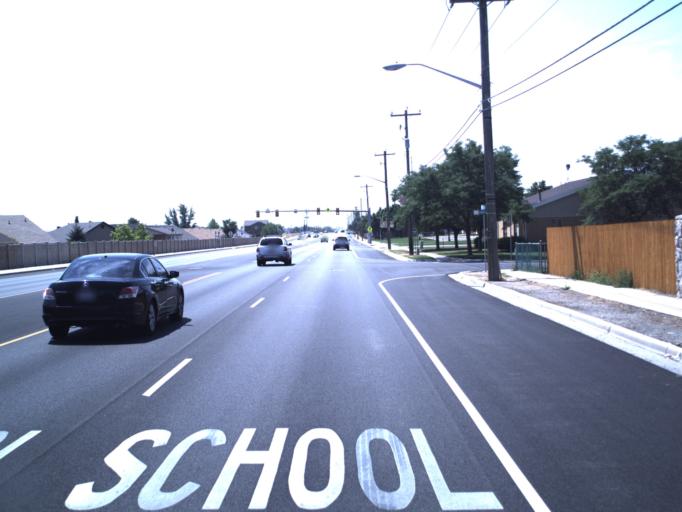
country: US
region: Utah
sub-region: Salt Lake County
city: Oquirrh
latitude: 40.6469
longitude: -112.0247
